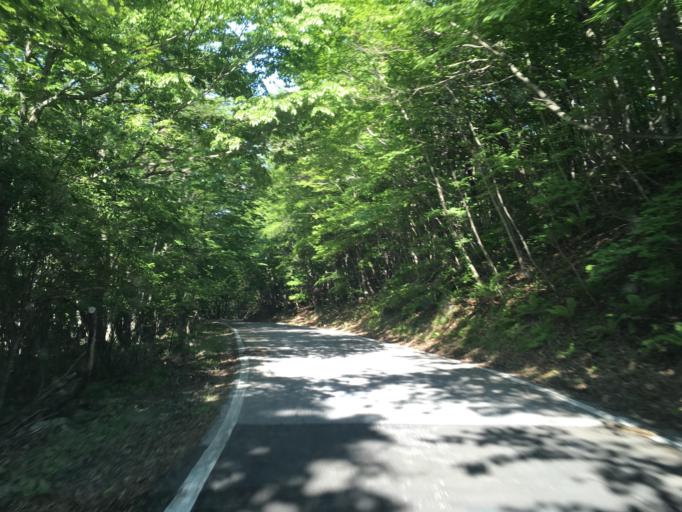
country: JP
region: Iwate
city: Ofunato
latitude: 39.1830
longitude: 141.7635
